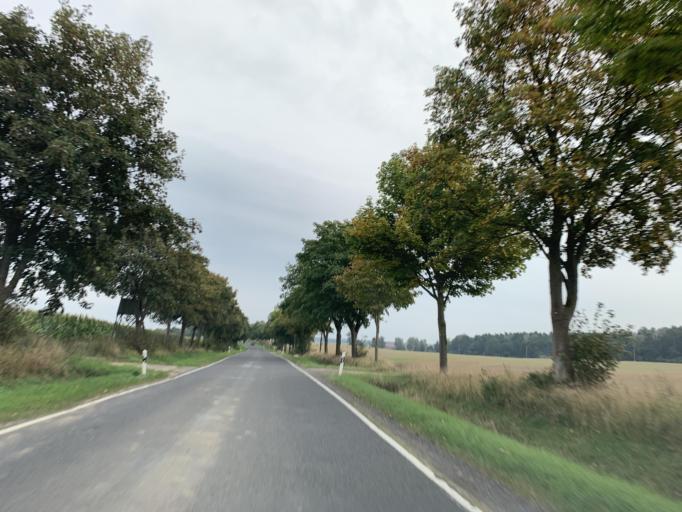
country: DE
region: Mecklenburg-Vorpommern
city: Woldegk
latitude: 53.3286
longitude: 13.5425
